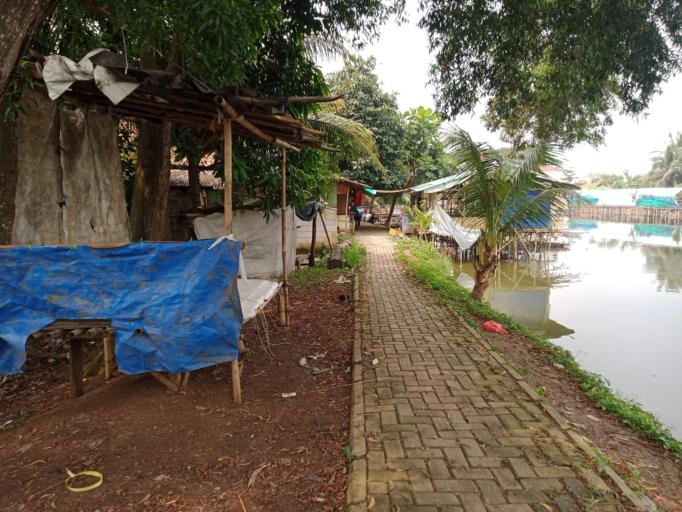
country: ID
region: West Java
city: Pasarkemis
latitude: -6.1985
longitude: 106.5251
